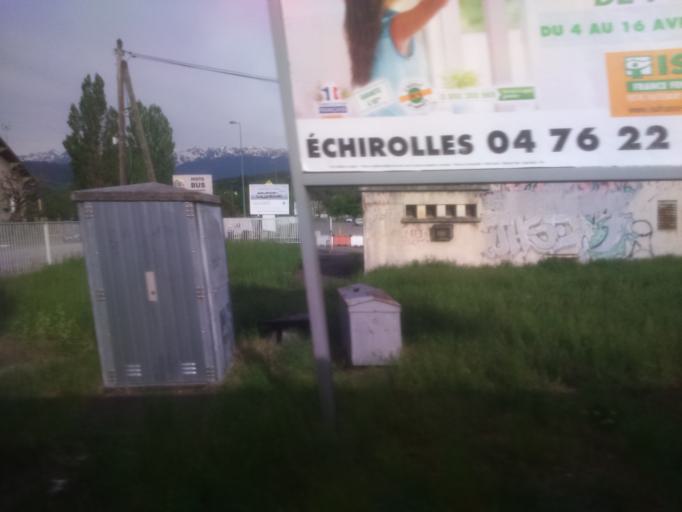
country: FR
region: Rhone-Alpes
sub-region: Departement de l'Isere
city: Le Pont-de-Claix
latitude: 45.1378
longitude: 5.7031
